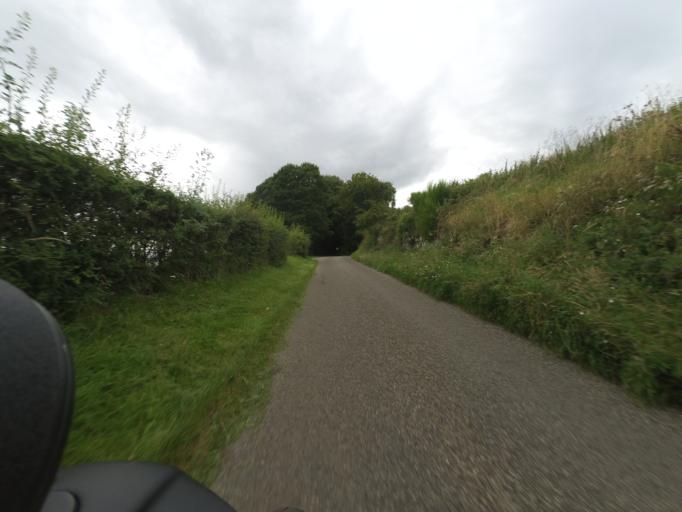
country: GB
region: Scotland
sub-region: Highland
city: Conon Bridge
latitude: 57.5124
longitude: -4.3839
